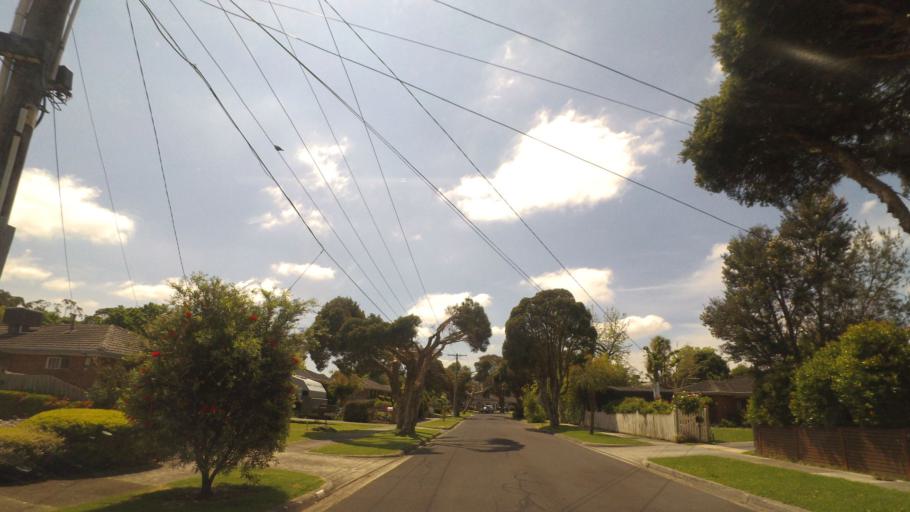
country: AU
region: Victoria
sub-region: Maroondah
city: Heathmont
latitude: -37.8340
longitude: 145.2632
